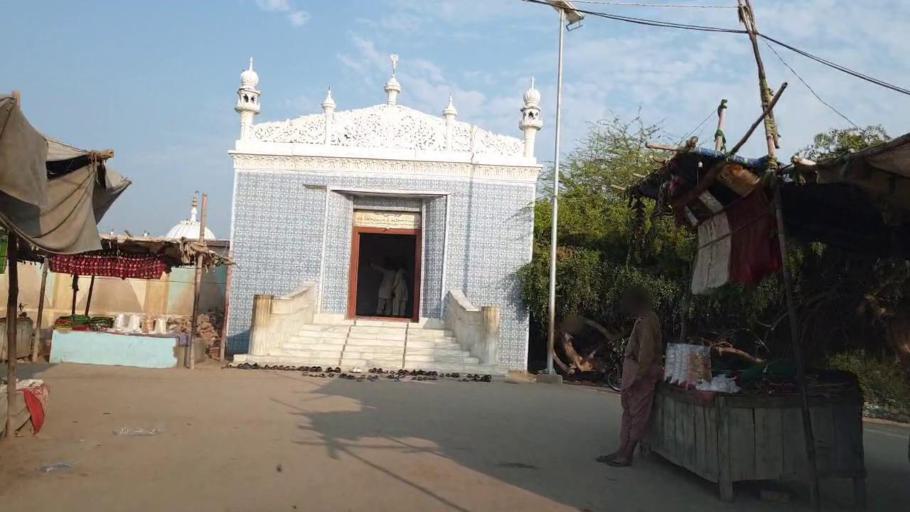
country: PK
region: Sindh
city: Pithoro
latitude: 25.5822
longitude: 69.3622
